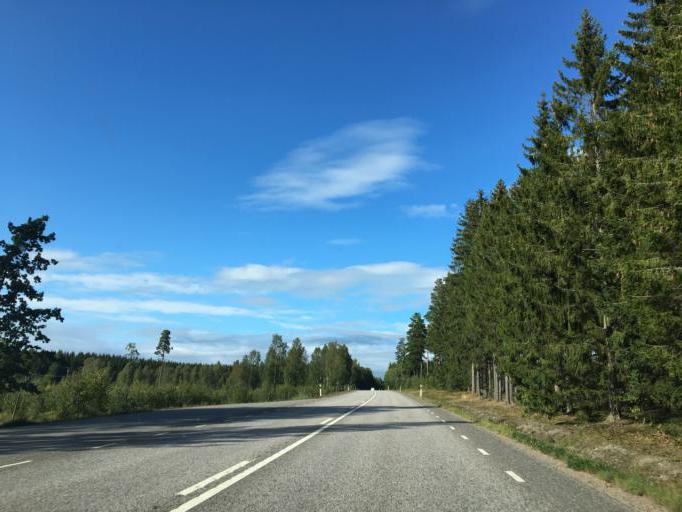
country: SE
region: Soedermanland
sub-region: Nykopings Kommun
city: Svalsta
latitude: 58.8397
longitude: 16.9230
